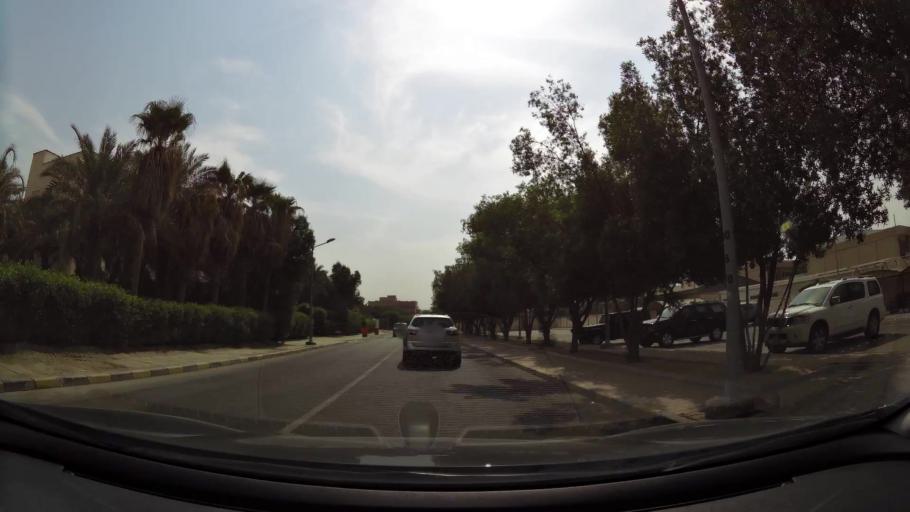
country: KW
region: Al Asimah
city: Ash Shamiyah
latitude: 29.3504
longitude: 47.9752
